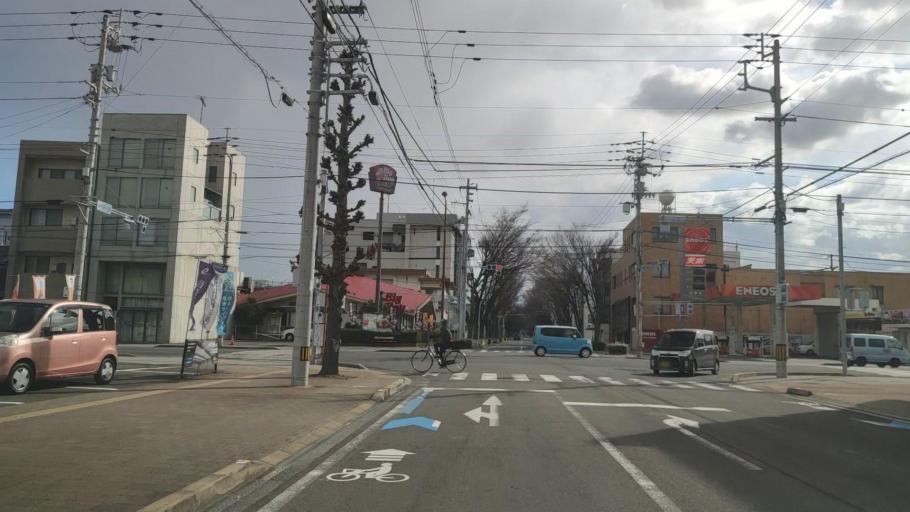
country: JP
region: Ehime
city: Hojo
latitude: 34.0633
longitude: 132.9963
